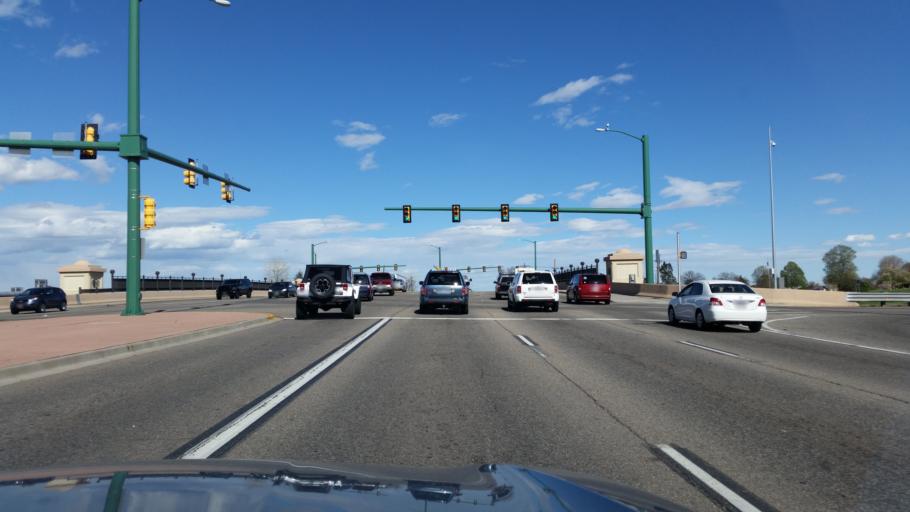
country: US
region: Colorado
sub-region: Adams County
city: Northglenn
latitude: 39.8852
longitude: -104.9889
